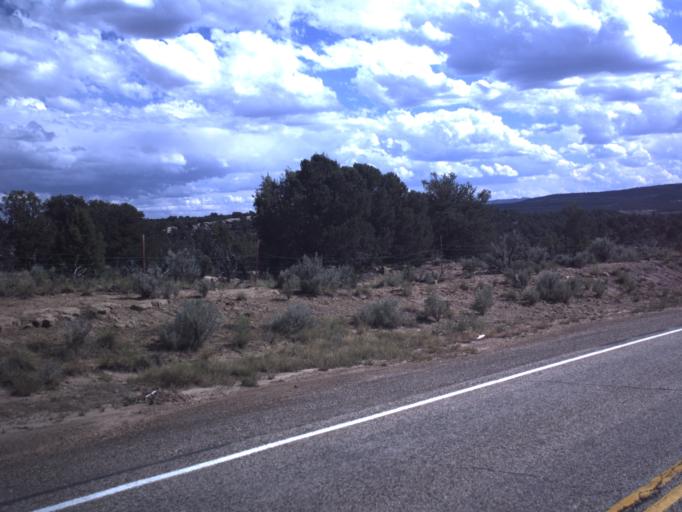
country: US
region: Utah
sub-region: Duchesne County
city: Duchesne
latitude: 40.2462
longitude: -110.7119
